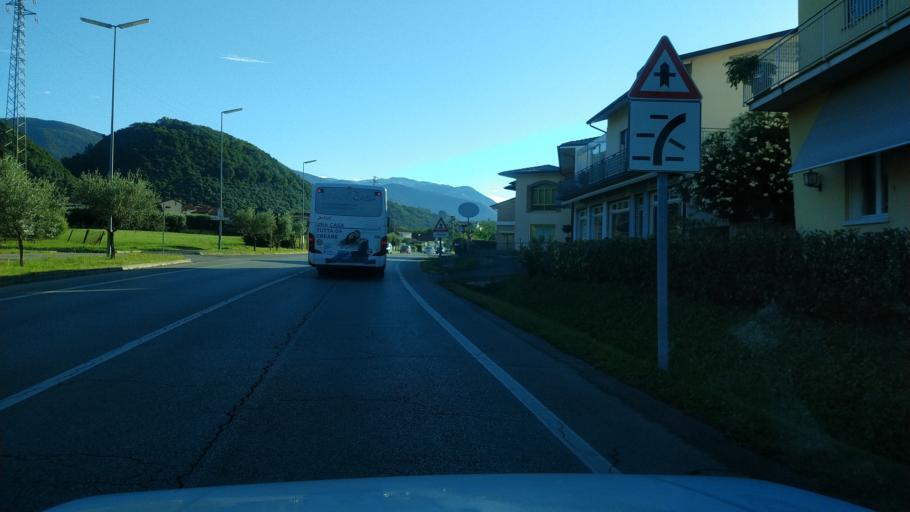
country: IT
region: Veneto
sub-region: Provincia di Vicenza
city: Marostica
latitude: 45.7580
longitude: 11.6861
